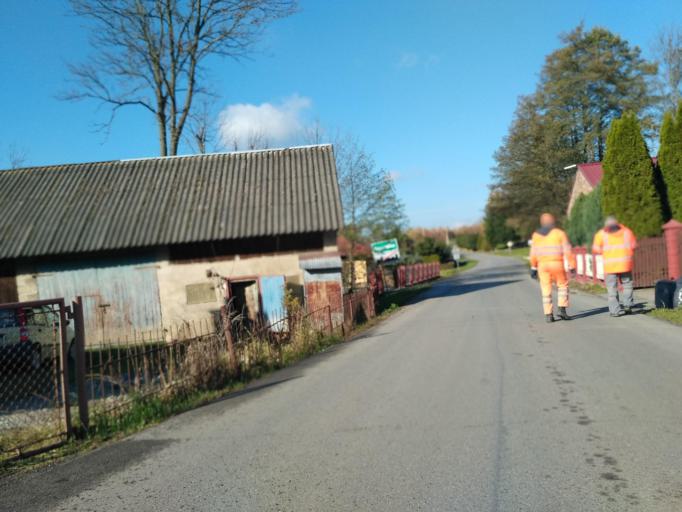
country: PL
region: Subcarpathian Voivodeship
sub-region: Powiat rzeszowski
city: Zglobien
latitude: 50.0305
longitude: 21.8610
